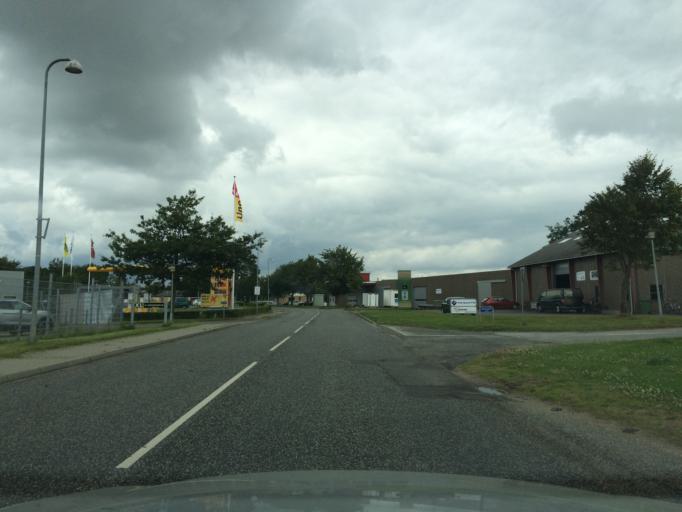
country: DK
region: Central Jutland
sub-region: Favrskov Kommune
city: Hammel
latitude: 56.2203
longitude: 9.7433
